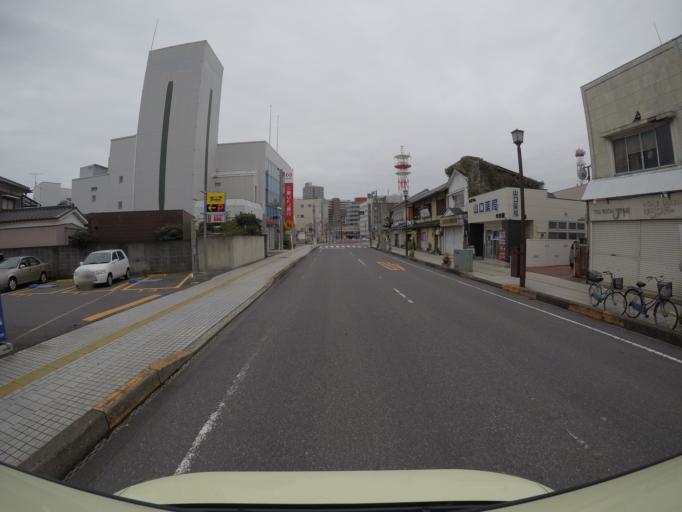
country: JP
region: Ibaraki
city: Naka
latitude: 36.0833
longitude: 140.2007
